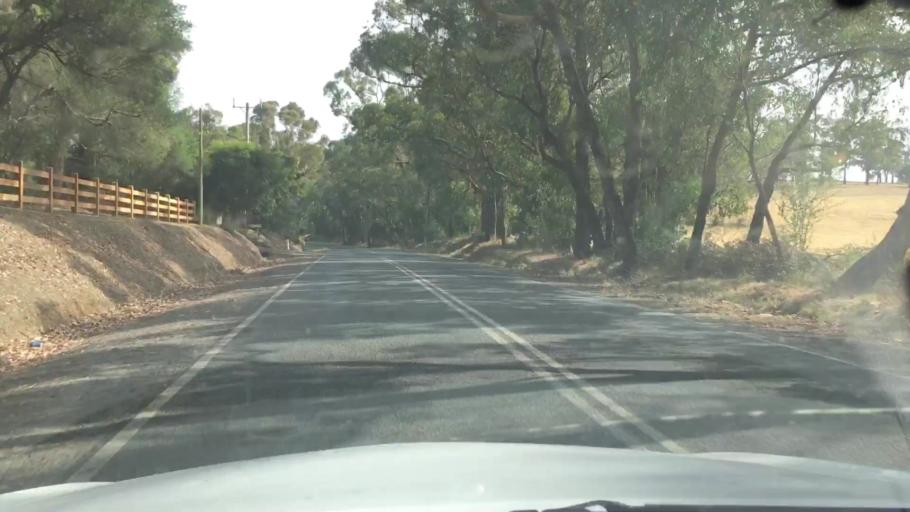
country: AU
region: Victoria
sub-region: Yarra Ranges
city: Macclesfield
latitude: -37.8704
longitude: 145.4793
